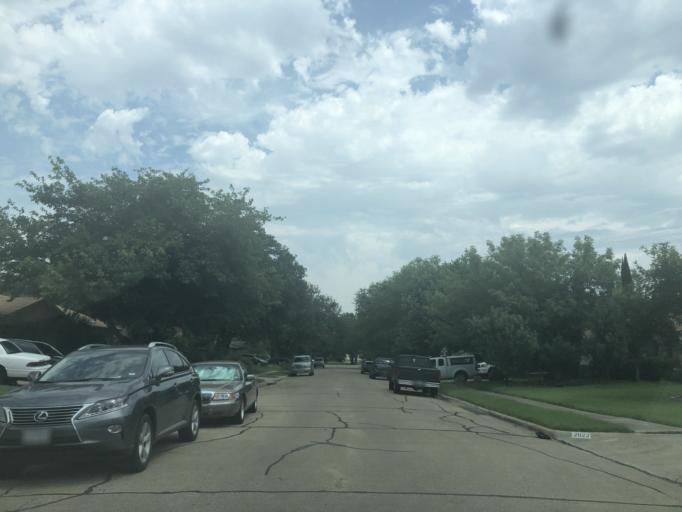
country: US
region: Texas
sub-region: Dallas County
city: Irving
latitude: 32.7927
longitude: -96.9372
